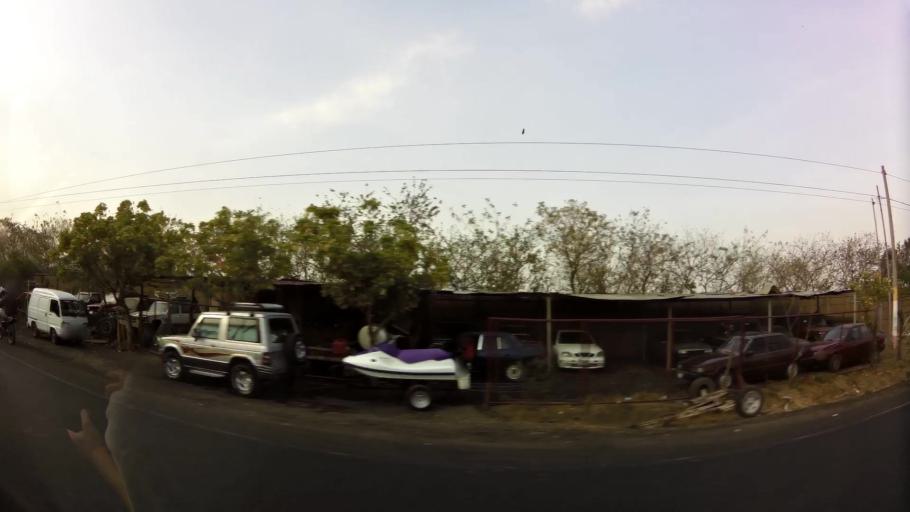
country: NI
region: Managua
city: Ciudad Sandino
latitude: 12.1358
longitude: -86.3271
